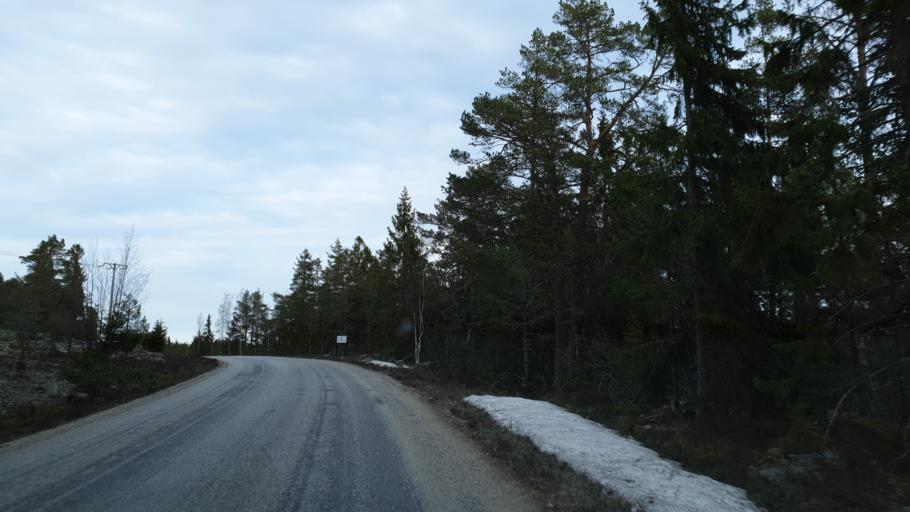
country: SE
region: Vaesternorrland
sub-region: Sundsvalls Kommun
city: Njurundabommen
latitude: 61.9671
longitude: 17.3787
